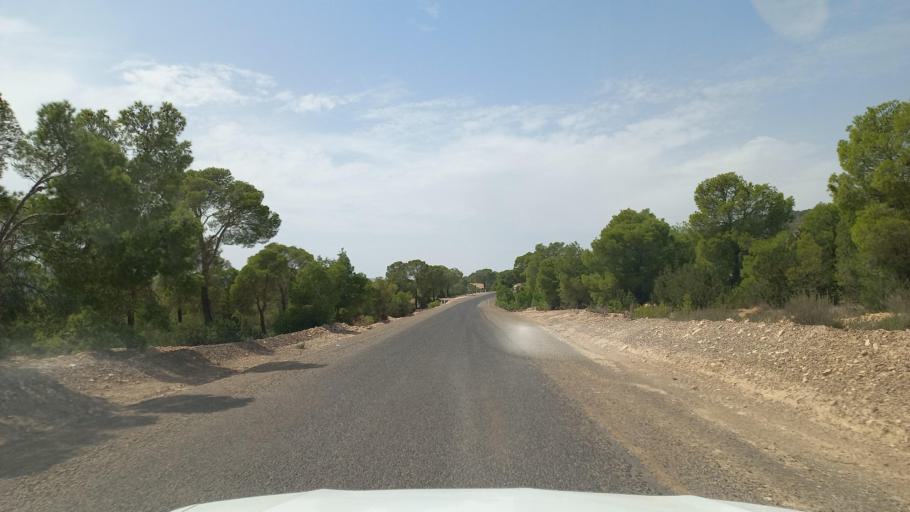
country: TN
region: Al Qasrayn
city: Sbiba
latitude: 35.3798
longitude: 8.9221
